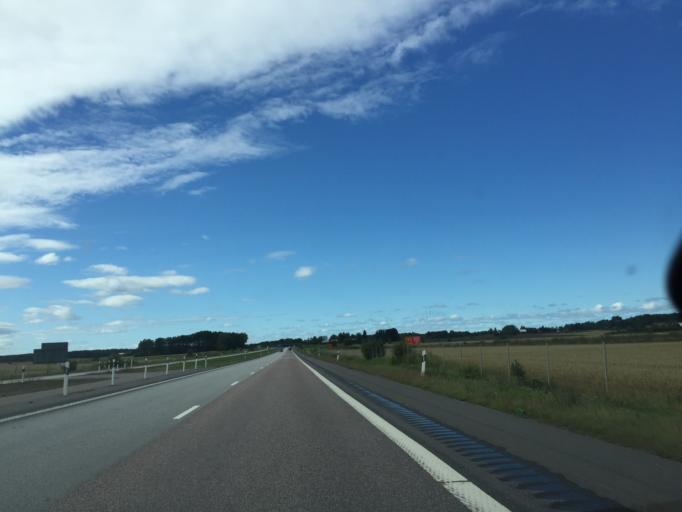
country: SE
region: OErebro
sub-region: Lindesbergs Kommun
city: Frovi
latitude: 59.3078
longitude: 15.3919
